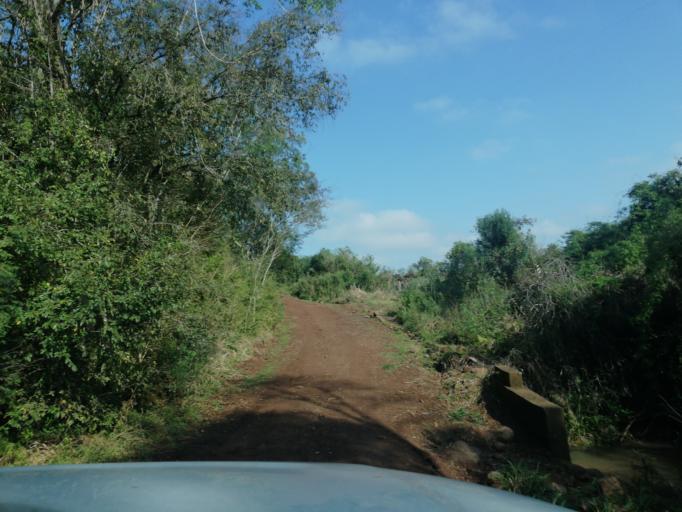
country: AR
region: Misiones
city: Cerro Azul
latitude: -27.5976
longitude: -55.5245
